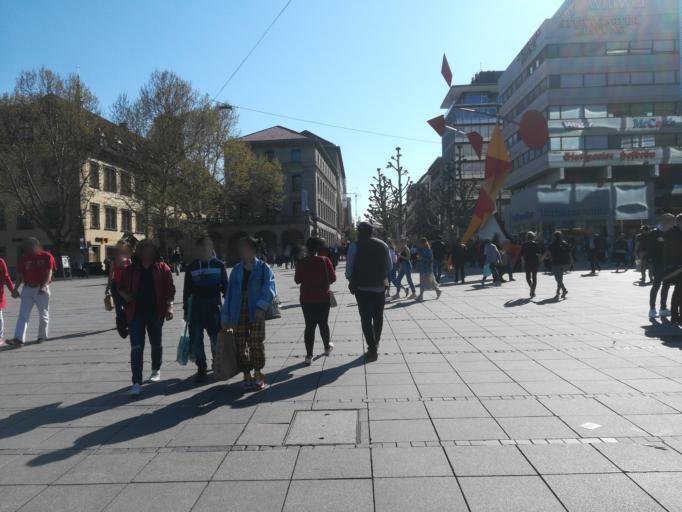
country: DE
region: Baden-Wuerttemberg
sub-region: Regierungsbezirk Stuttgart
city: Stuttgart
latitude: 48.7785
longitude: 9.1783
